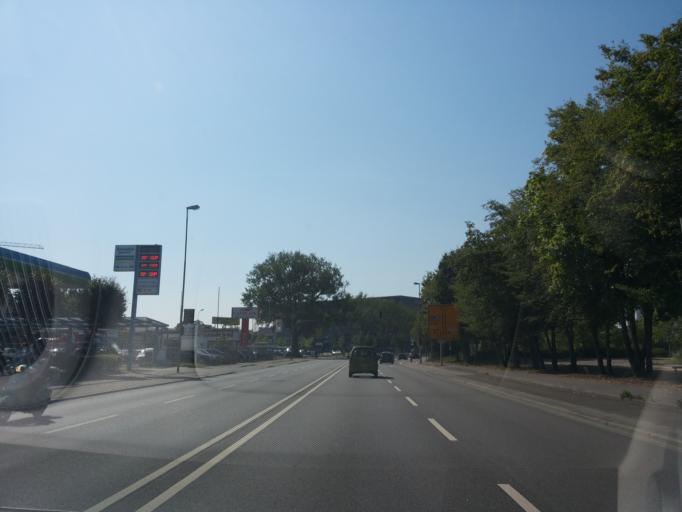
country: DE
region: Bavaria
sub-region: Upper Bavaria
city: Ingolstadt
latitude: 48.7614
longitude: 11.4403
